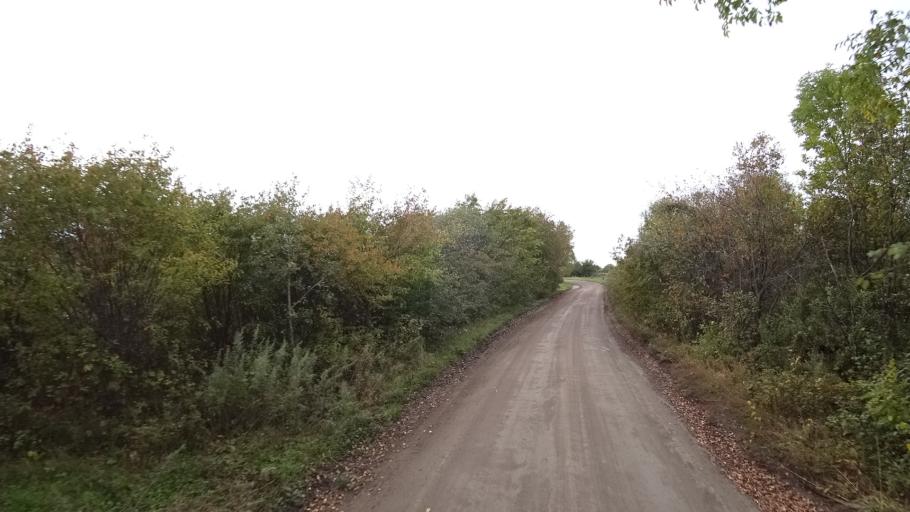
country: RU
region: Amur
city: Arkhara
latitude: 49.3563
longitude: 130.1270
